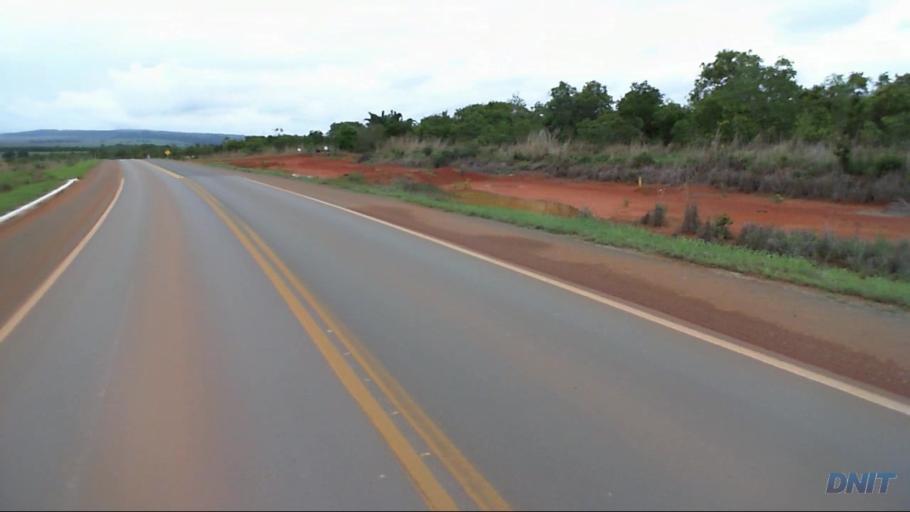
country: BR
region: Goias
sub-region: Padre Bernardo
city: Padre Bernardo
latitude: -15.1503
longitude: -48.3460
